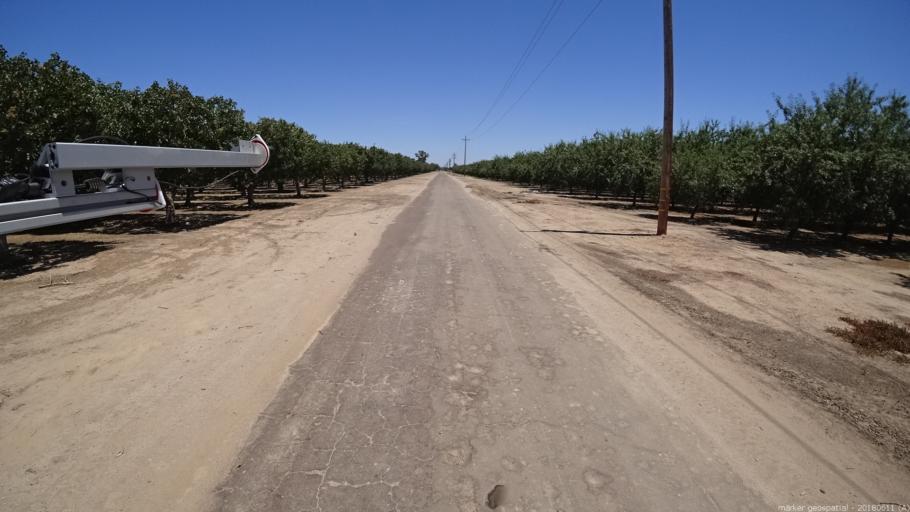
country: US
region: California
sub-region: Madera County
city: Fairmead
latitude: 37.0692
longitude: -120.2197
